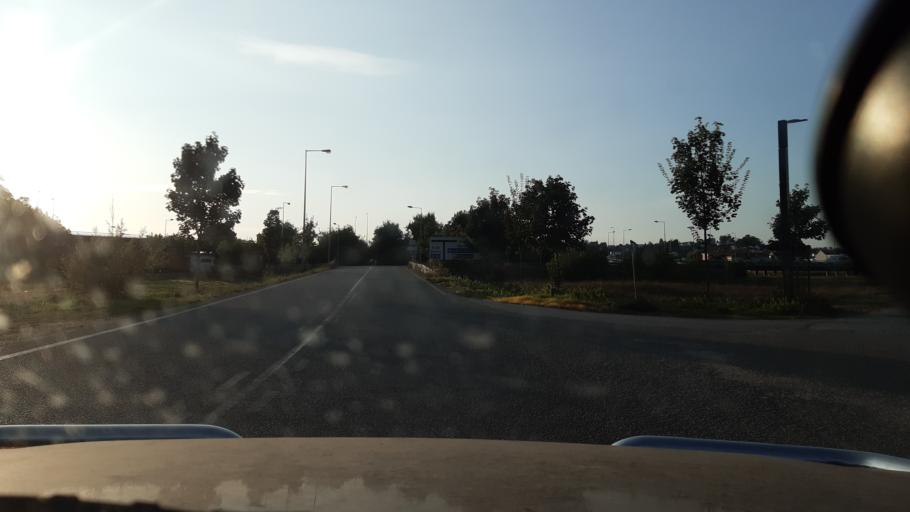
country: PT
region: Aveiro
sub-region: Agueda
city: Agueda
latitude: 40.5659
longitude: -8.4467
